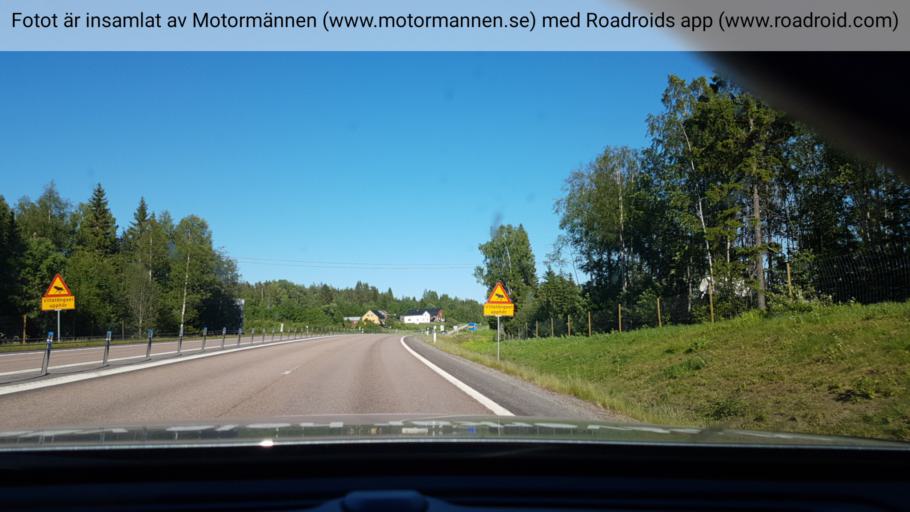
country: SE
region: Vaesternorrland
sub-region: Timra Kommun
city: Soraker
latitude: 62.5583
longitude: 17.6513
